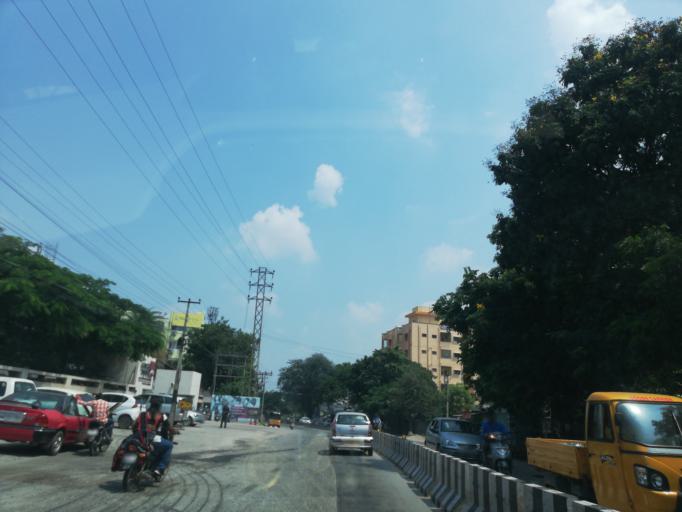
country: IN
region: Telangana
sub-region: Medak
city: Serilingampalle
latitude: 17.4823
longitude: 78.3204
